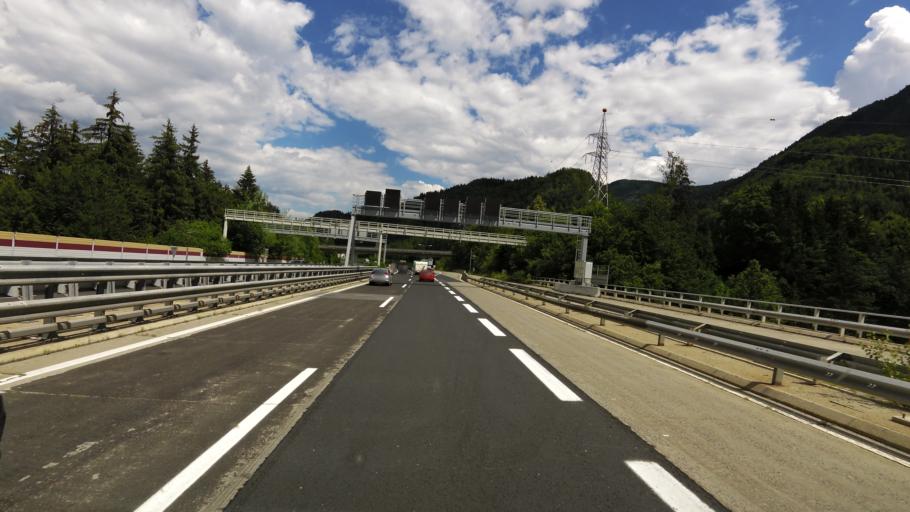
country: AT
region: Carinthia
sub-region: Politischer Bezirk Villach Land
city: Hohenthurn
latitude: 46.5382
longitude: 13.6586
